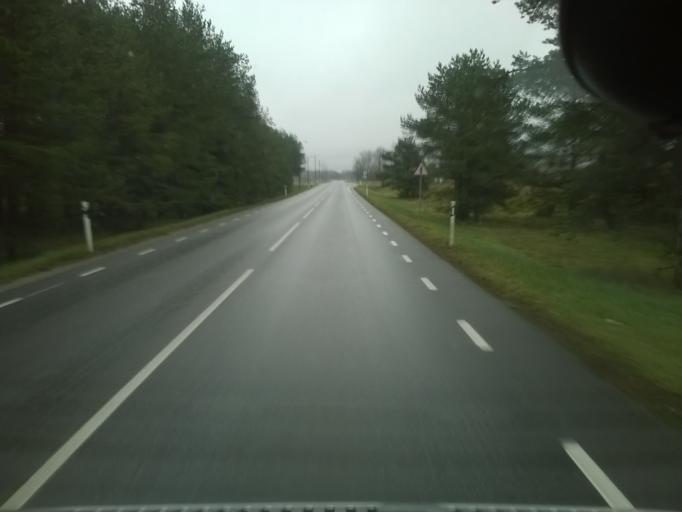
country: EE
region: Harju
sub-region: Saku vald
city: Saku
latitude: 59.2677
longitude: 24.7328
